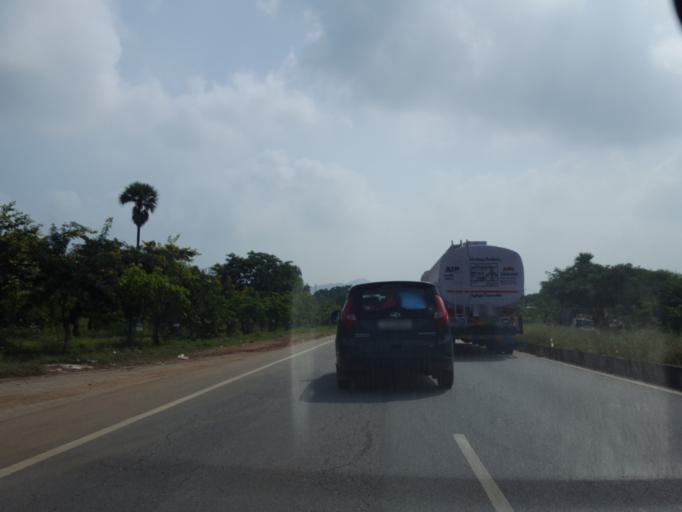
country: IN
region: Telangana
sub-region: Rangareddi
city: Ghatkesar
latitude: 17.2928
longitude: 78.7525
